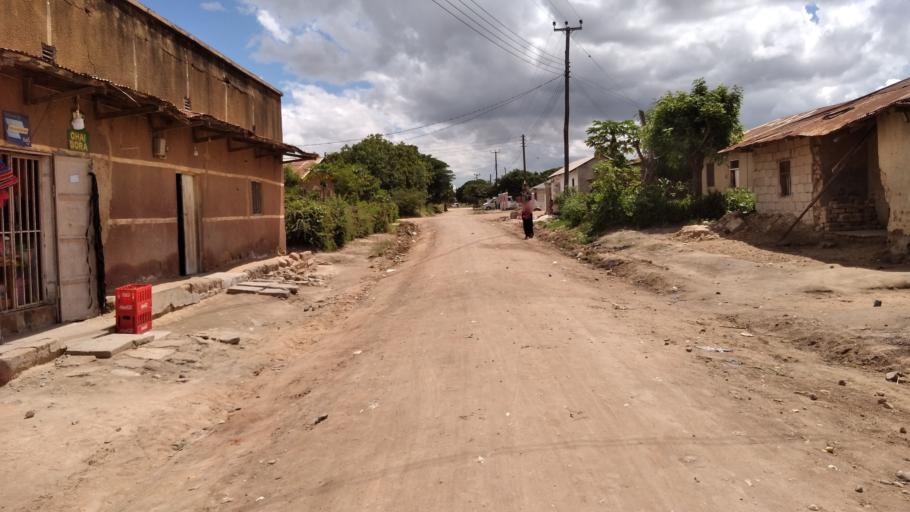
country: TZ
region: Dodoma
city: Dodoma
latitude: -6.1635
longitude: 35.7391
